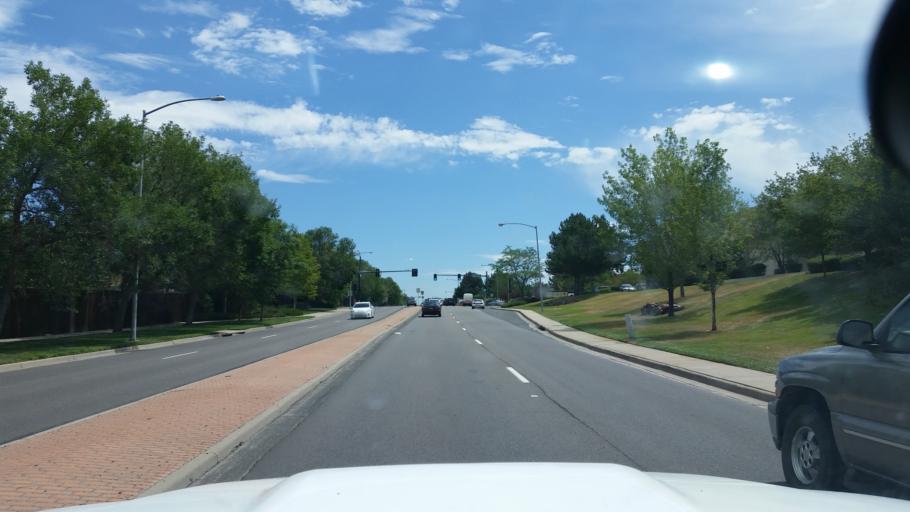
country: US
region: Colorado
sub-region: Adams County
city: Westminster
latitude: 39.8637
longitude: -105.0675
